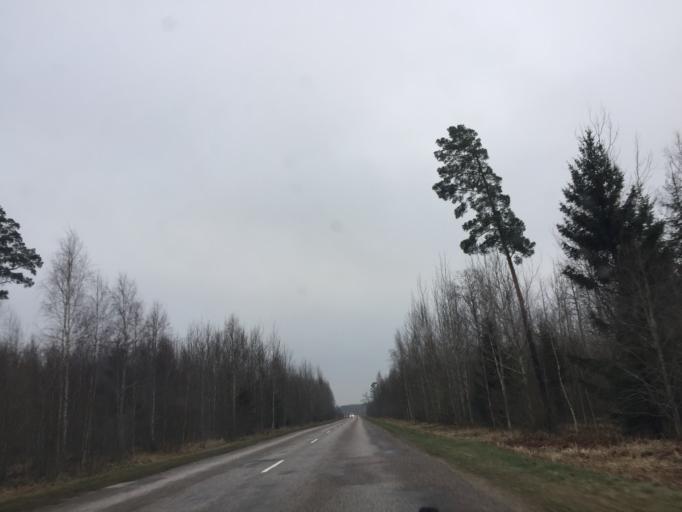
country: LV
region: Limbazu Rajons
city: Limbazi
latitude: 57.5588
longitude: 24.6685
